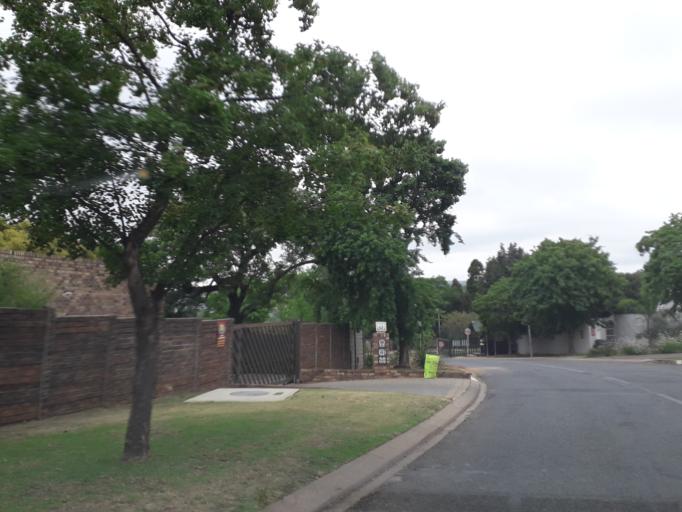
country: ZA
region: Gauteng
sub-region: City of Johannesburg Metropolitan Municipality
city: Roodepoort
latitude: -26.1107
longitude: 27.9437
